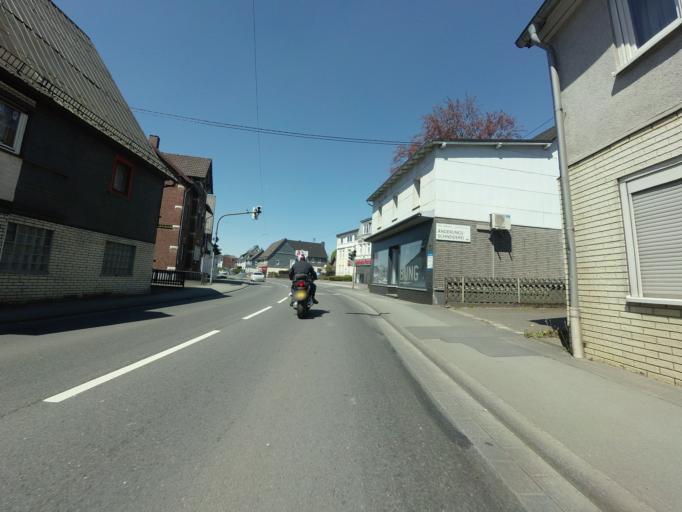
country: DE
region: North Rhine-Westphalia
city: Kreuztal
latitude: 50.9610
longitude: 8.0071
